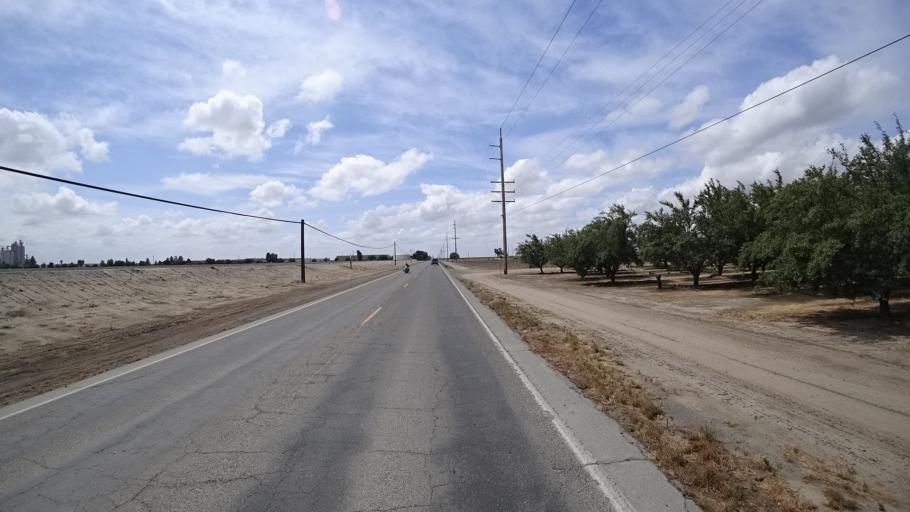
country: US
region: California
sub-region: Kings County
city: Home Garden
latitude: 36.2880
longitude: -119.6549
